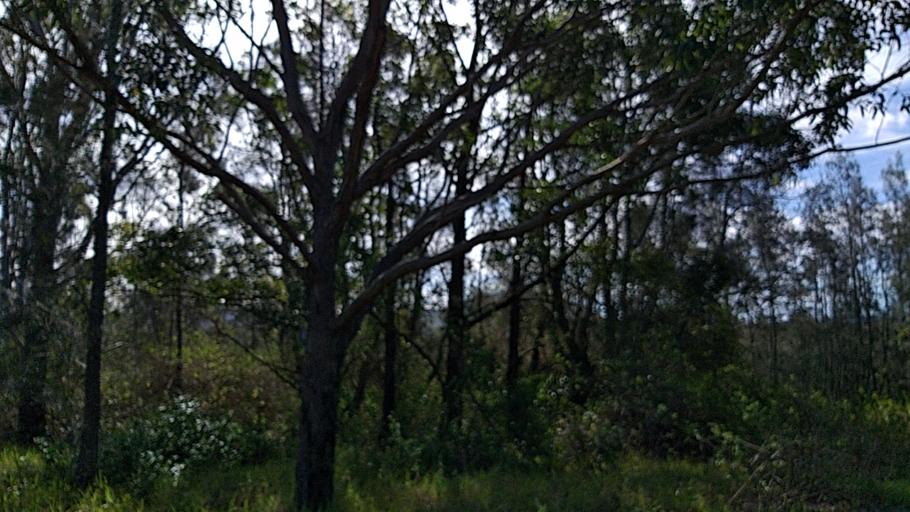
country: AU
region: New South Wales
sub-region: Wollongong
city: Berkeley
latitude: -34.4869
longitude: 150.8350
